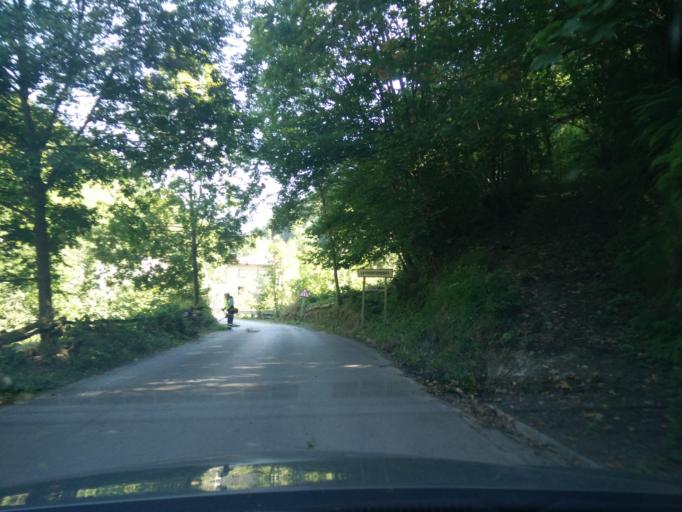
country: ES
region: Asturias
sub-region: Province of Asturias
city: Campo de Caso
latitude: 43.1690
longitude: -5.3929
